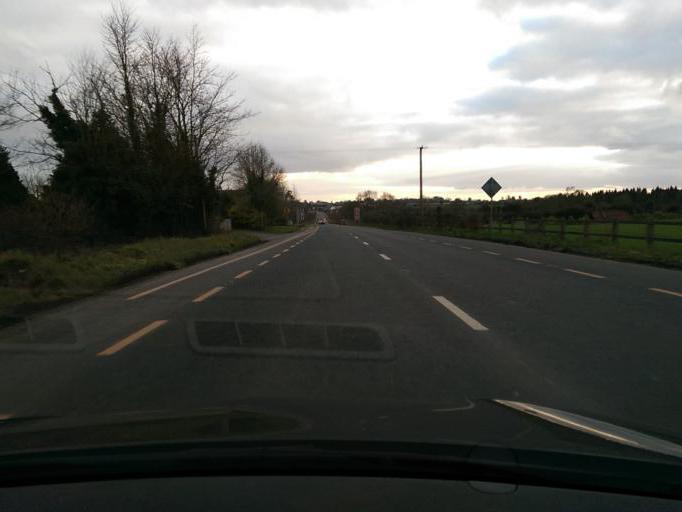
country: IE
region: Leinster
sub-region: Uibh Fhaili
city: Birr
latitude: 53.1103
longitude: -7.8984
